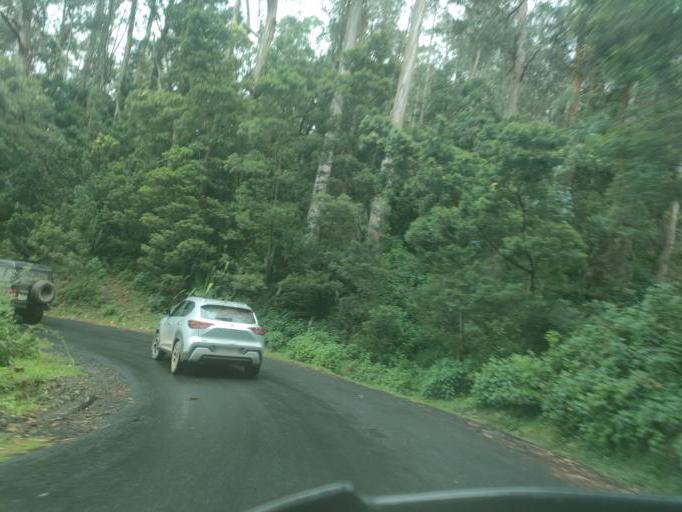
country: IN
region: Tamil Nadu
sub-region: Dindigul
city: Kodaikanal
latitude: 10.2423
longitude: 77.3581
